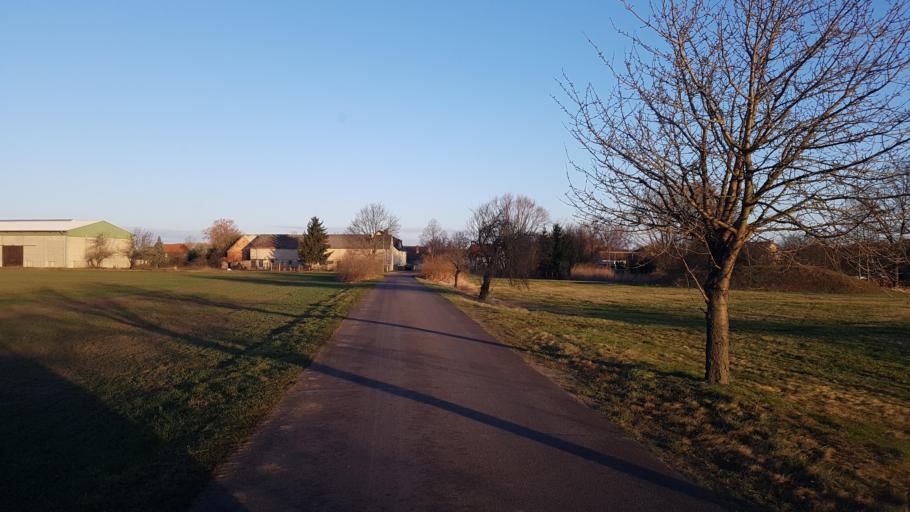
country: DE
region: Brandenburg
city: Falkenberg
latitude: 51.6332
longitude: 13.2402
